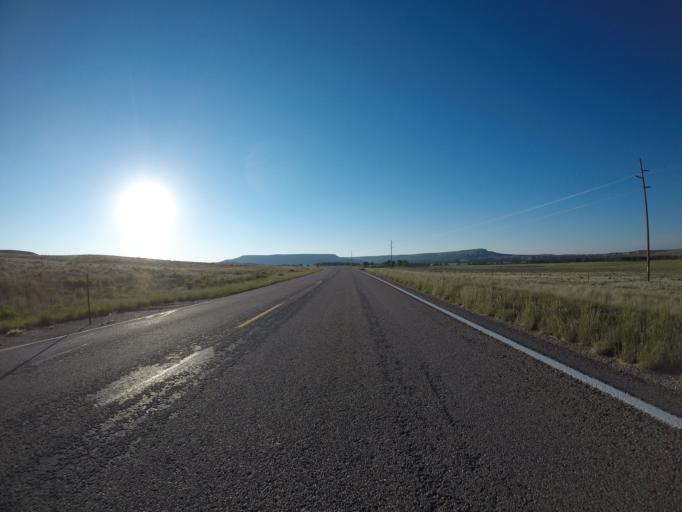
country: US
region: Wyoming
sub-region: Sublette County
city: Marbleton
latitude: 42.5722
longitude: -109.9744
